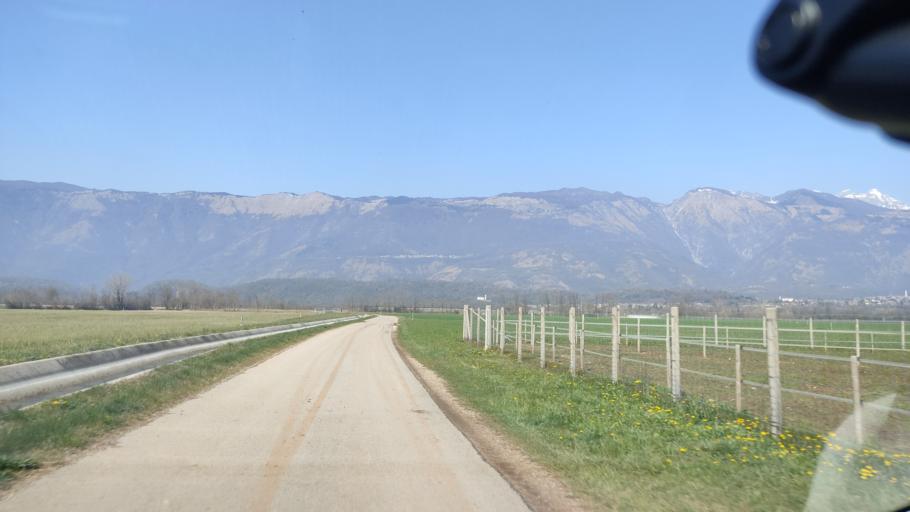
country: IT
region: Friuli Venezia Giulia
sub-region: Provincia di Pordenone
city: Budoia
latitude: 46.0200
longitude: 12.5464
